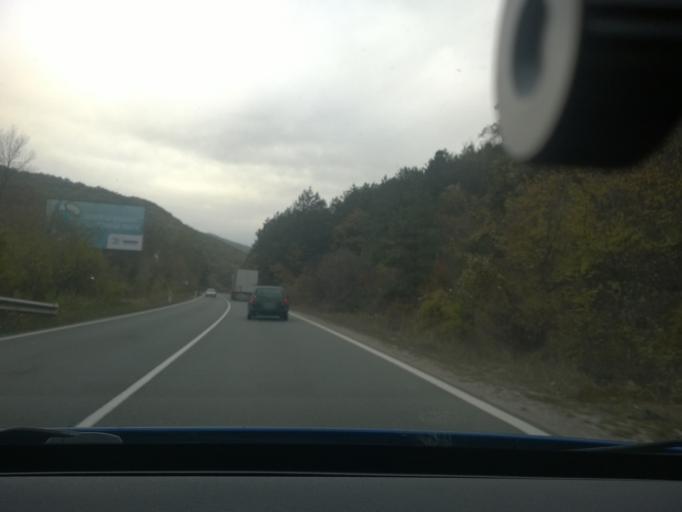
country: BG
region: Sofiya
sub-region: Obshtina Dragoman
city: Dragoman
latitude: 42.9638
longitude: 22.8831
